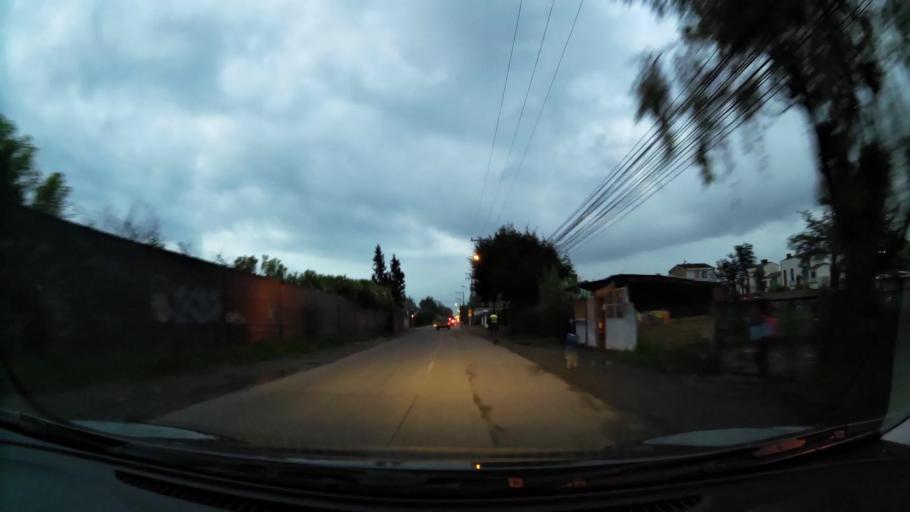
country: CO
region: Cundinamarca
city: Chia
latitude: 4.8456
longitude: -74.0658
